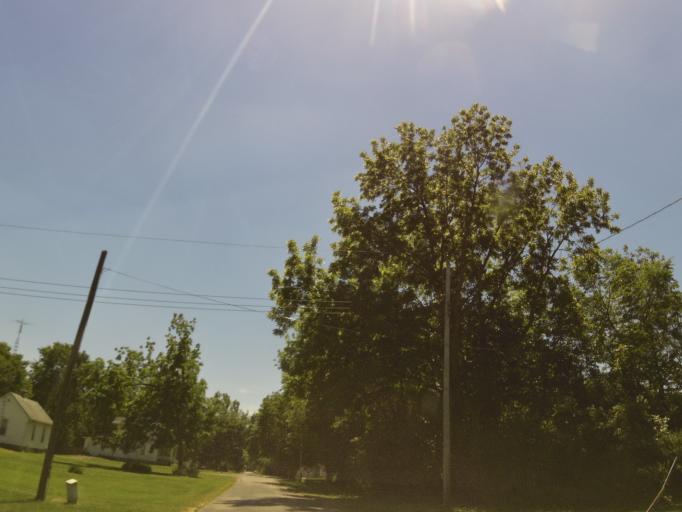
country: US
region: Illinois
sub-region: Livingston County
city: Chatsworth
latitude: 40.7581
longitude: -88.1851
